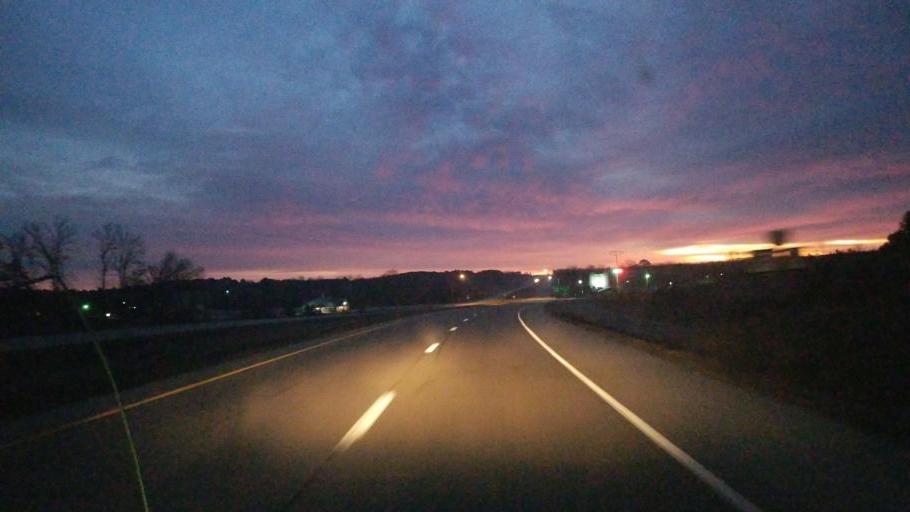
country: US
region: Missouri
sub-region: Shannon County
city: Winona
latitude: 36.9994
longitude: -91.4971
